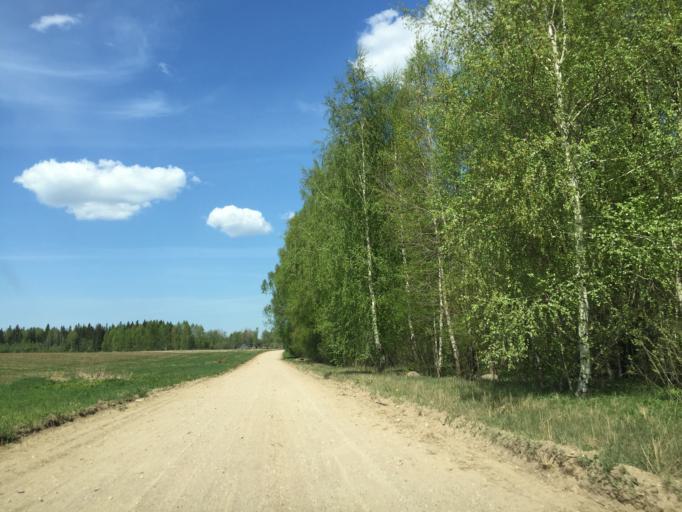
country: LV
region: Limbazu Rajons
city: Limbazi
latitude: 57.3605
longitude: 24.6403
